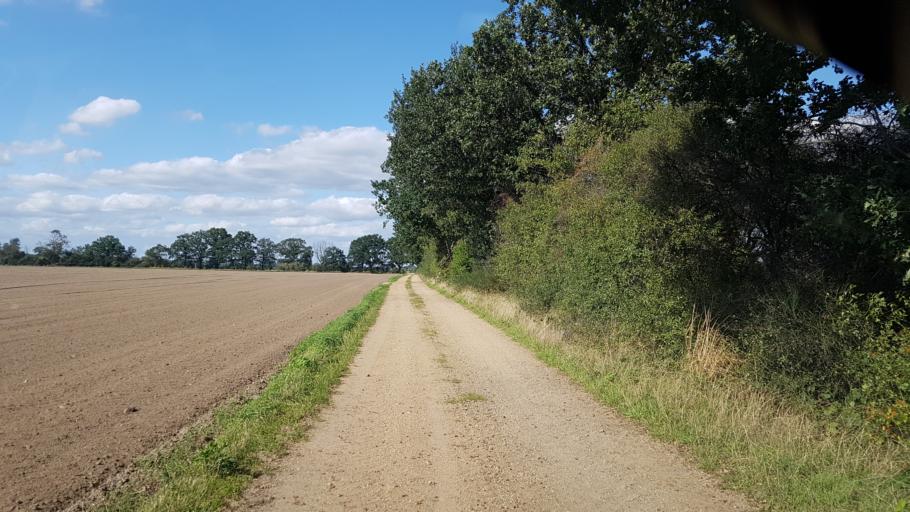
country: DE
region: Brandenburg
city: Sonnewalde
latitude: 51.6856
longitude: 13.6640
